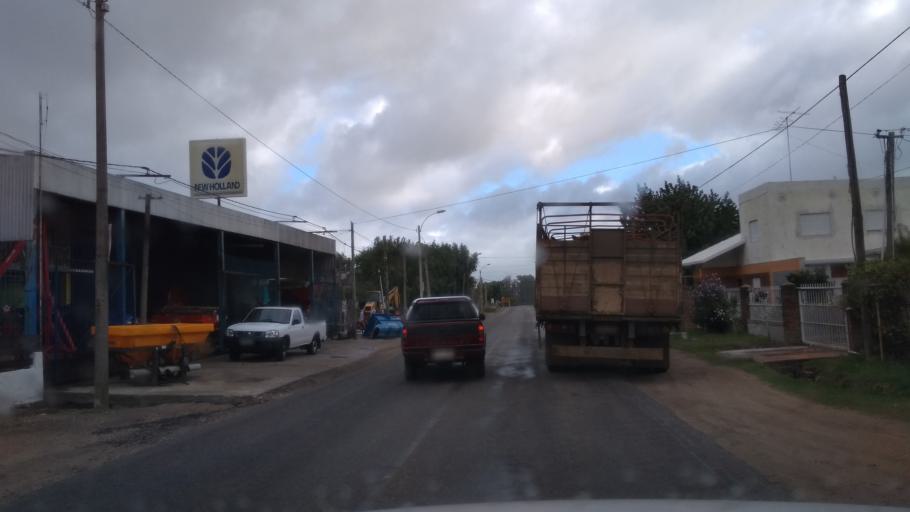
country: UY
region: Canelones
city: Tala
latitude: -34.3467
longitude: -55.7597
